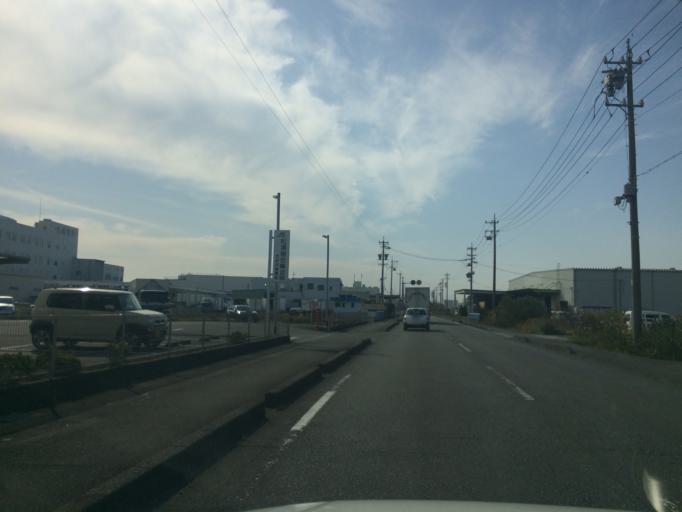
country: JP
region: Shizuoka
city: Fujieda
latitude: 34.7857
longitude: 138.2895
